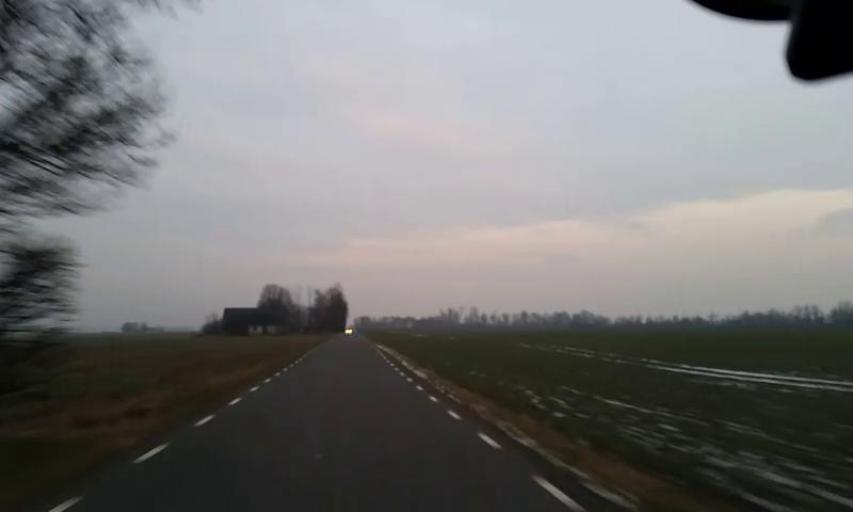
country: SE
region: Skane
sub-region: Angelholms Kommun
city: AEngelholm
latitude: 56.2784
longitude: 12.8673
